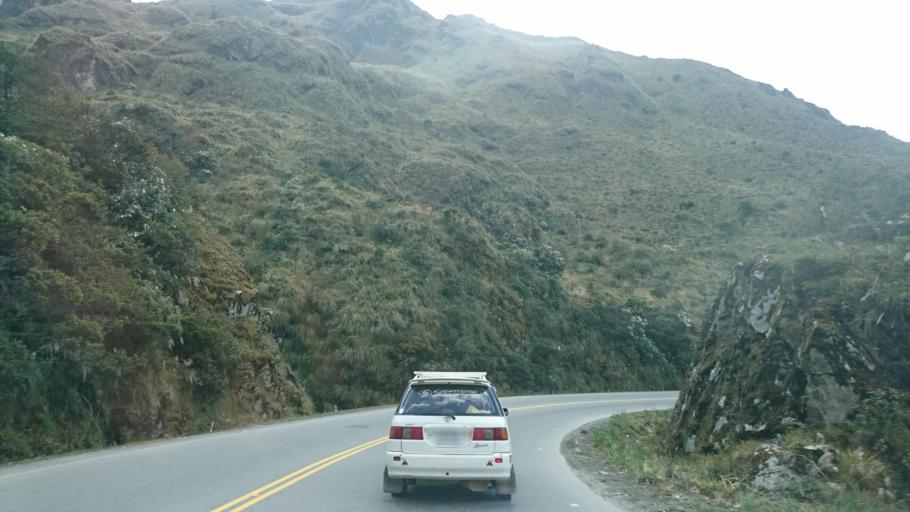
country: BO
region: La Paz
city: Coroico
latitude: -16.3153
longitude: -67.9256
